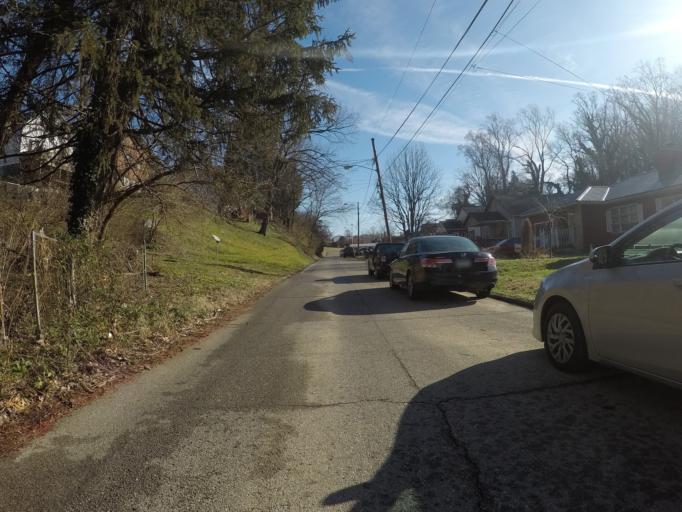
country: US
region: West Virginia
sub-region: Cabell County
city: Huntington
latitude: 38.4085
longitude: -82.4203
